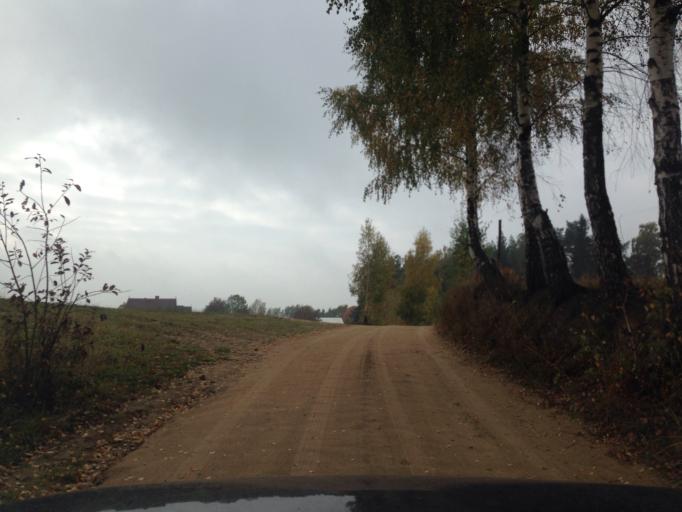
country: PL
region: Kujawsko-Pomorskie
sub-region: Powiat brodnicki
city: Gorzno
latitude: 53.2730
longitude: 19.7044
